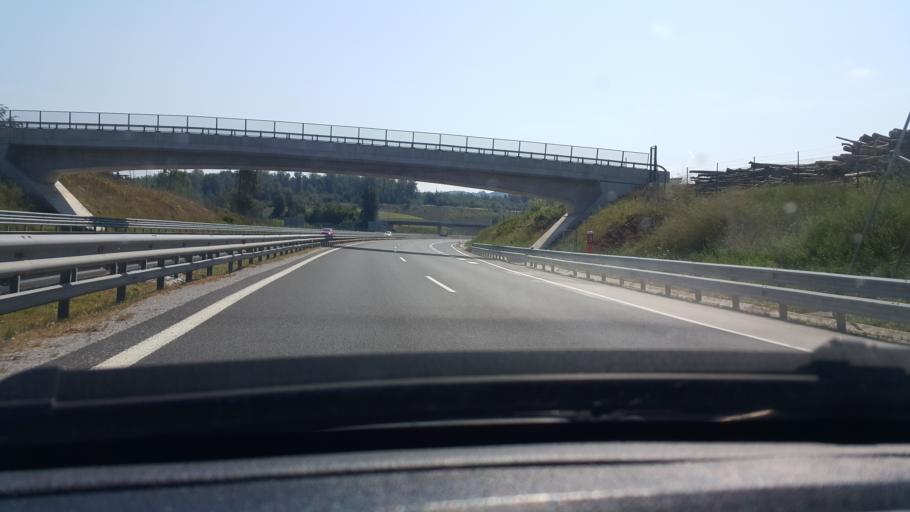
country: SI
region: Trebnje
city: Trebnje
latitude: 45.8999
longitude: 15.0509
